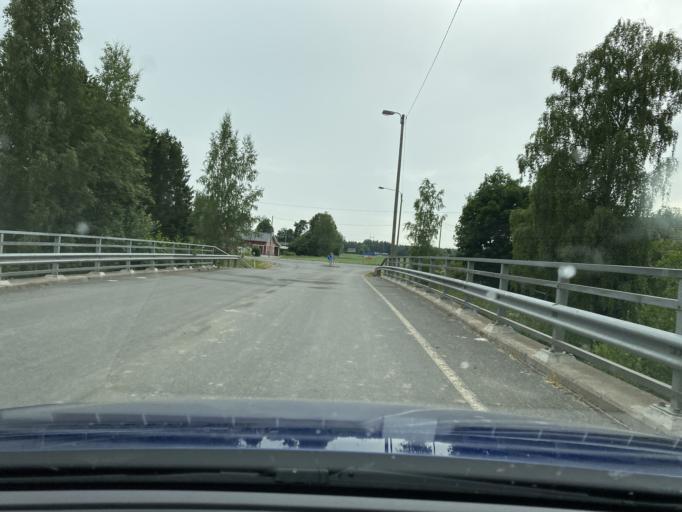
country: FI
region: Satakunta
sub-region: Rauma
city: Eura
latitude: 61.1426
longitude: 22.1198
